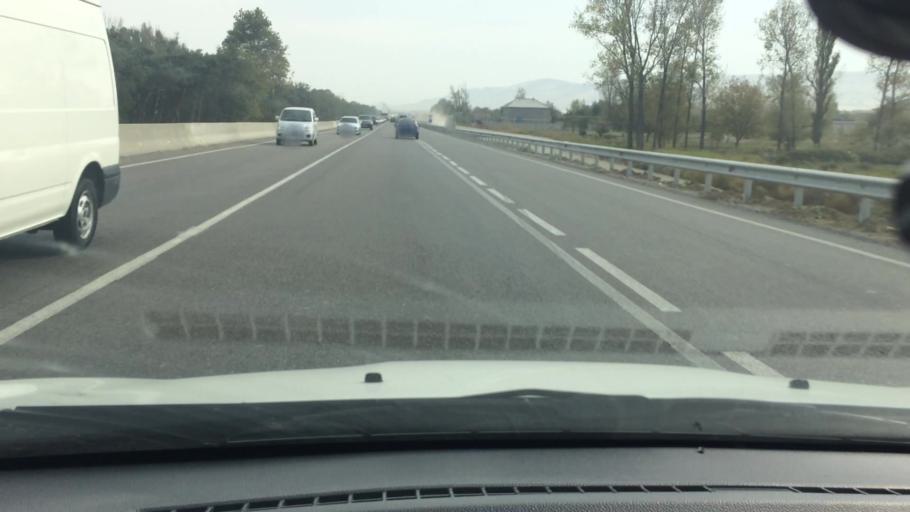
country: GE
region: Kvemo Kartli
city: Rust'avi
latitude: 41.6258
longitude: 44.9239
